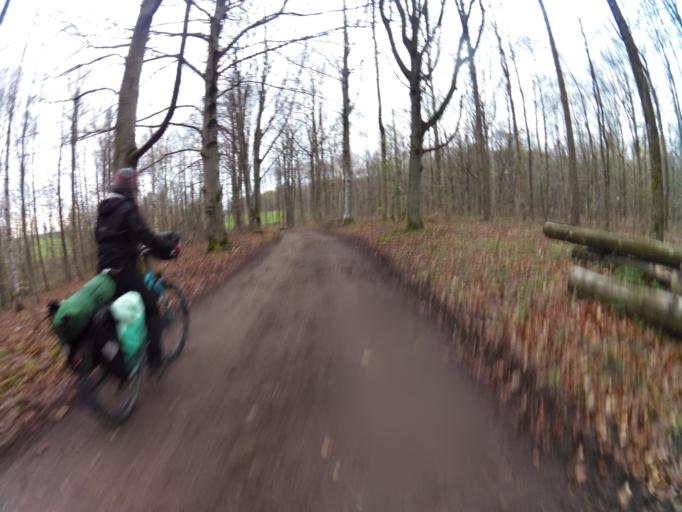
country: PL
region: West Pomeranian Voivodeship
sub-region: Powiat szczecinecki
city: Borne Sulinowo
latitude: 53.6502
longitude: 16.5071
